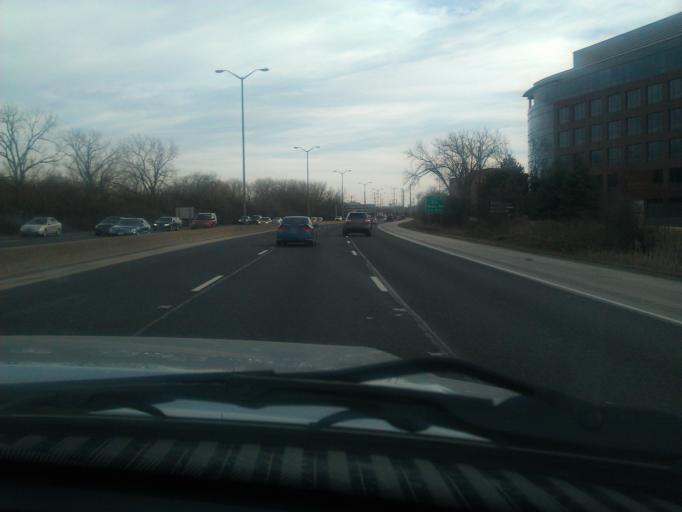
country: US
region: Illinois
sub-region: Cook County
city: Glencoe
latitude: 42.1336
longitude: -87.7858
